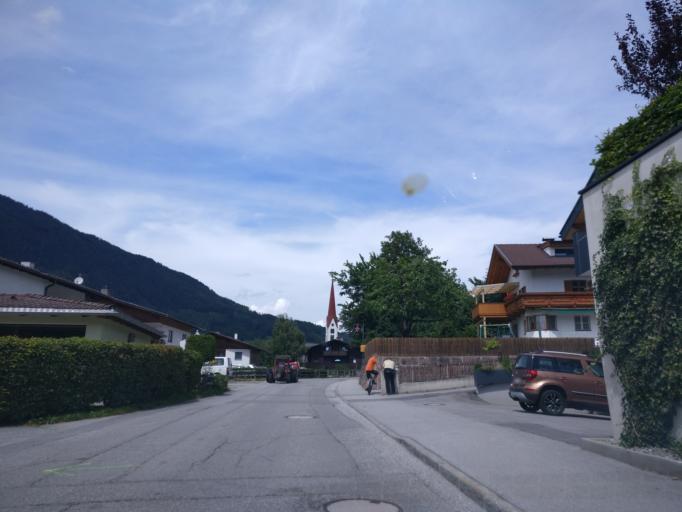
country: AT
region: Tyrol
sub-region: Politischer Bezirk Innsbruck Land
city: Mieders
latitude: 47.1664
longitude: 11.3794
